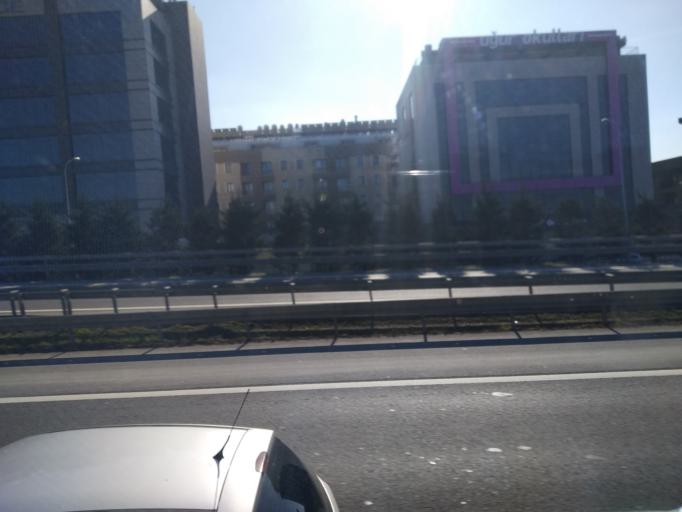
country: TR
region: Istanbul
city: Sultanbeyli
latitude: 40.9725
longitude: 29.2545
